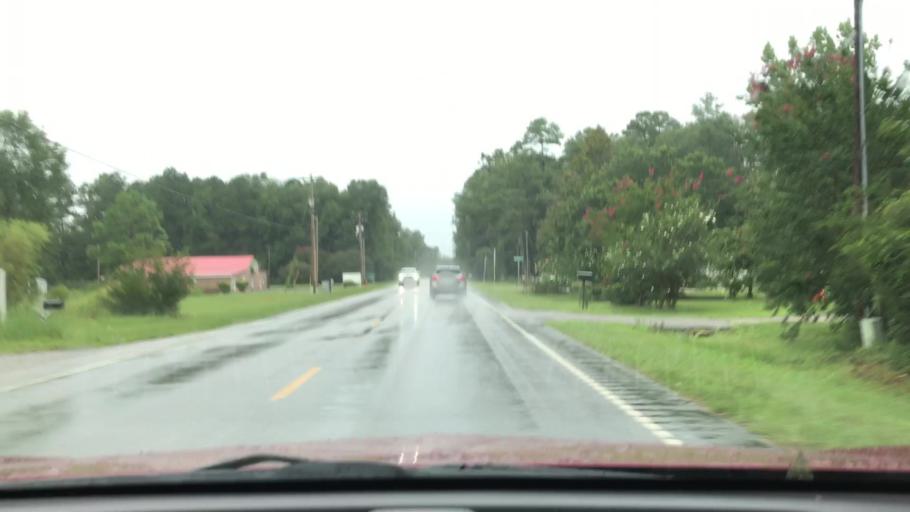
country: US
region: South Carolina
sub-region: Horry County
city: Conway
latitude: 33.7859
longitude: -79.0753
